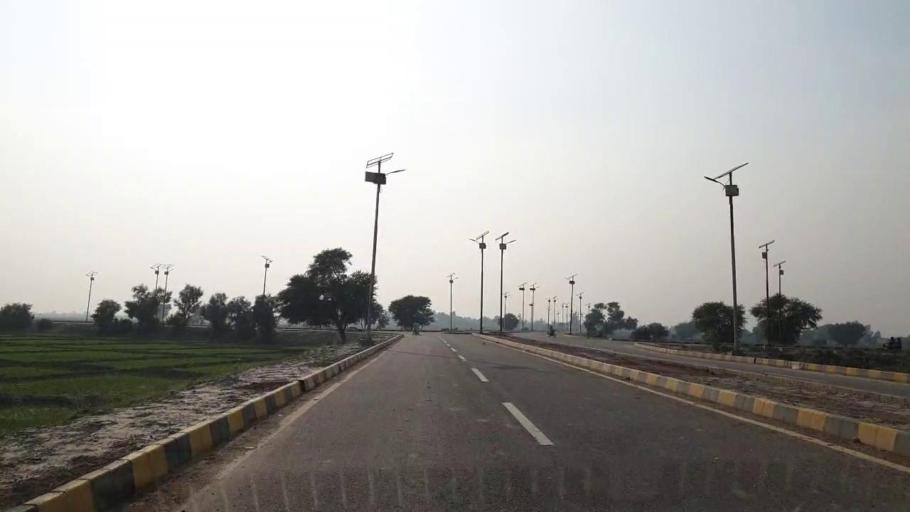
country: PK
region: Sindh
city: Bhan
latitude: 26.4760
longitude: 67.7258
